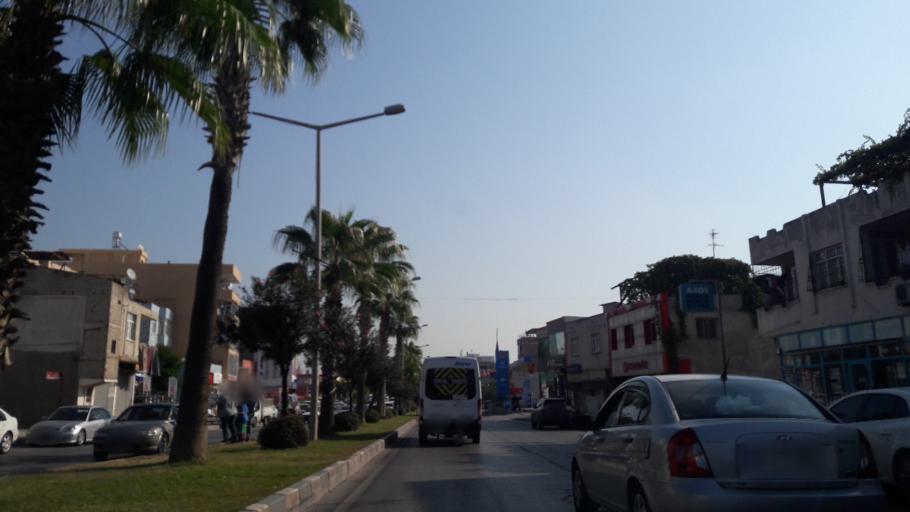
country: TR
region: Adana
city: Yuregir
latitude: 37.0339
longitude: 35.4142
